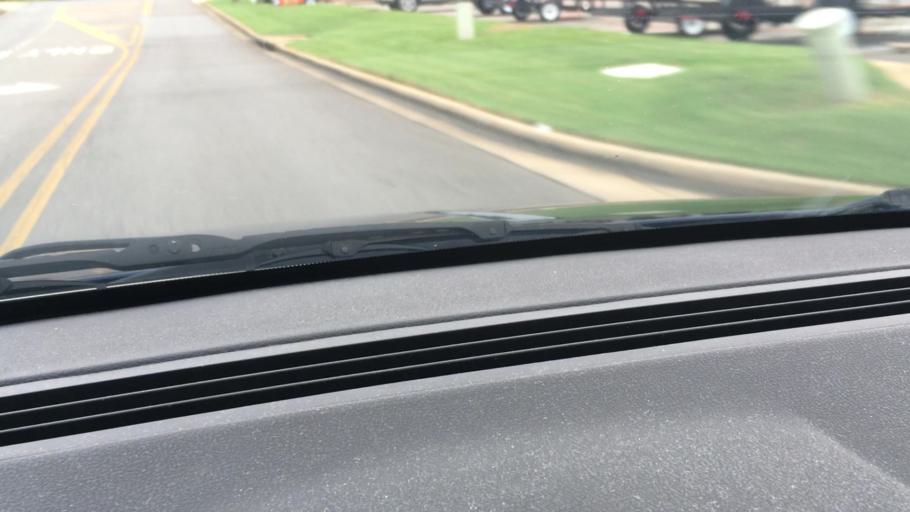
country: US
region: Alabama
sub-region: Tuscaloosa County
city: Tuscaloosa
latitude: 33.1949
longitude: -87.5193
